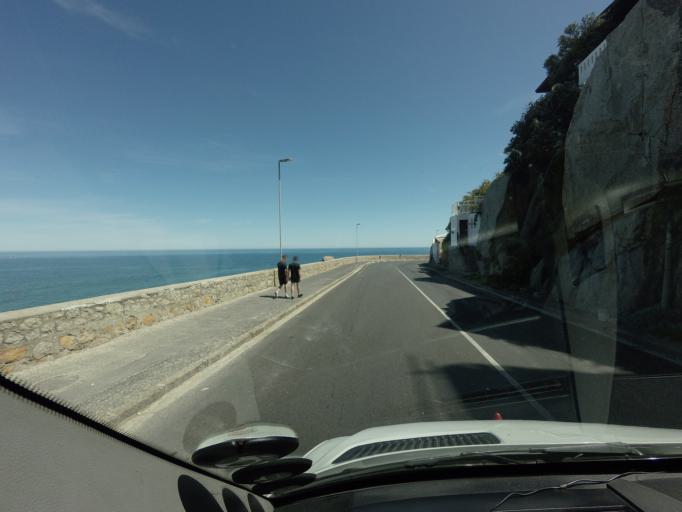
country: ZA
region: Western Cape
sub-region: City of Cape Town
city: Cape Town
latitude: -33.9299
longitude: 18.3757
